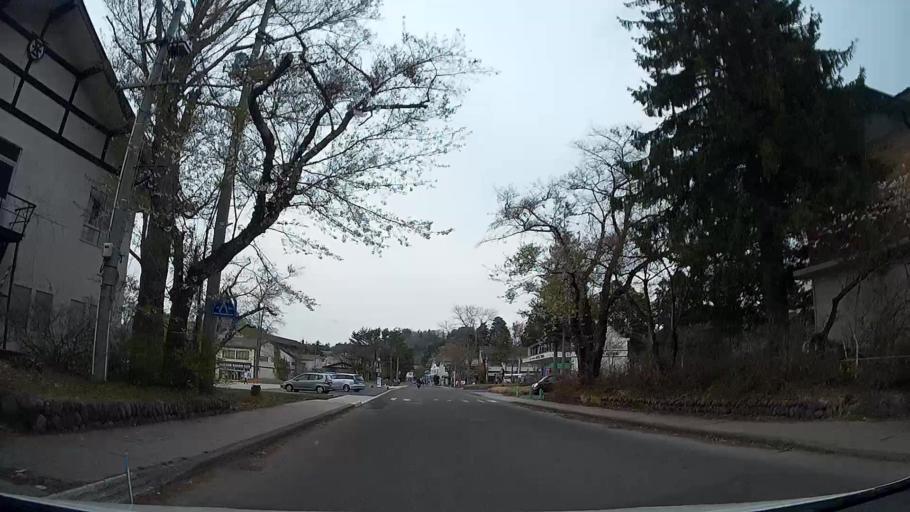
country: JP
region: Akita
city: Hanawa
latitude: 40.4257
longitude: 140.8940
